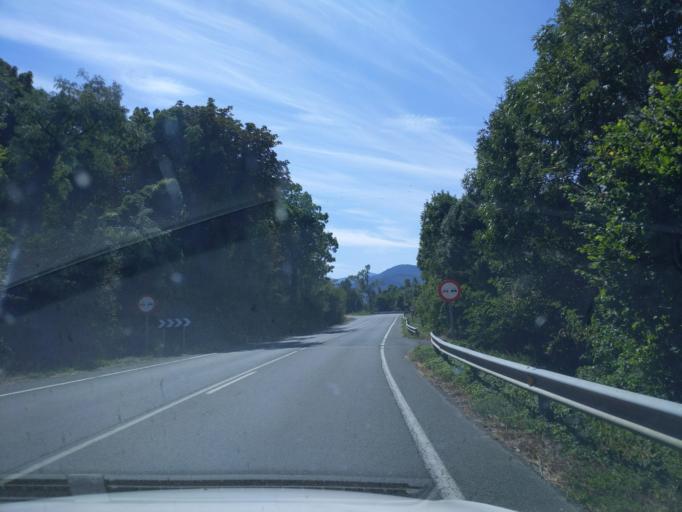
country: ES
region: La Rioja
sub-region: Provincia de La Rioja
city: Ojacastro
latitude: 42.3541
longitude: -2.9937
